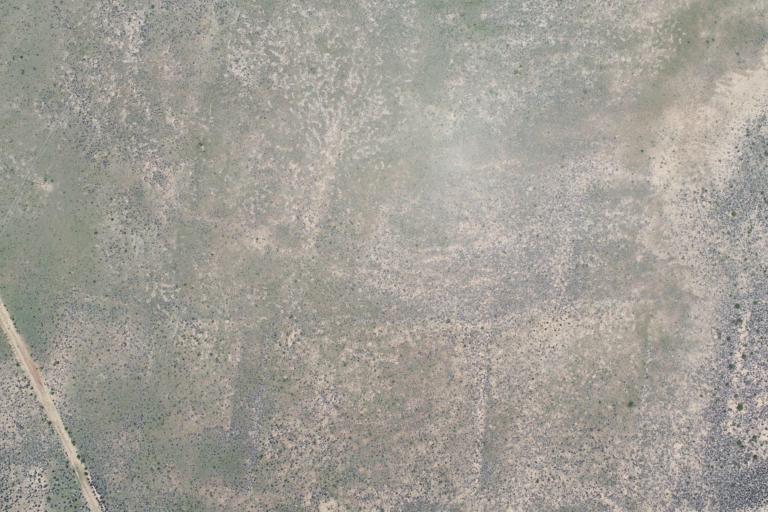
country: BO
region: La Paz
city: Curahuara de Carangas
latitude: -17.3095
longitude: -68.5125
